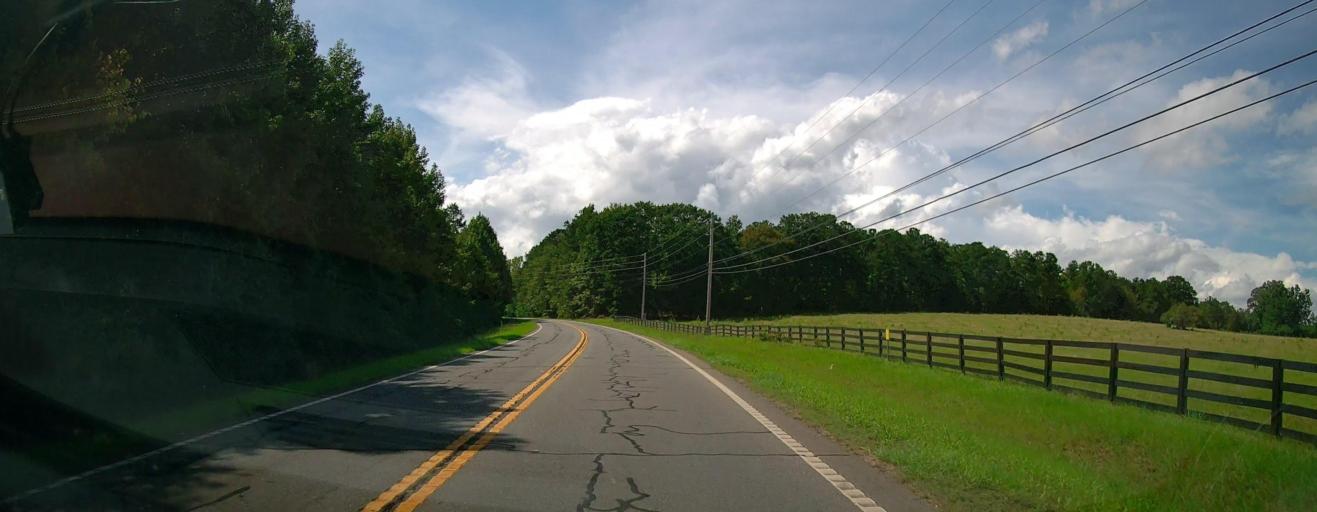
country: US
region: Georgia
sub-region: Talbot County
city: Sardis
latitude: 32.7969
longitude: -84.5705
